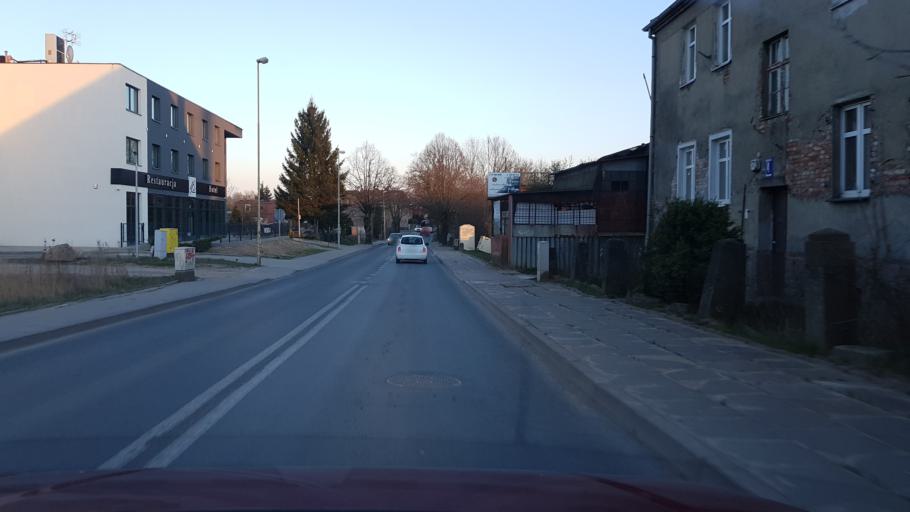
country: PL
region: West Pomeranian Voivodeship
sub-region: Szczecin
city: Szczecin
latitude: 53.4754
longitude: 14.5452
